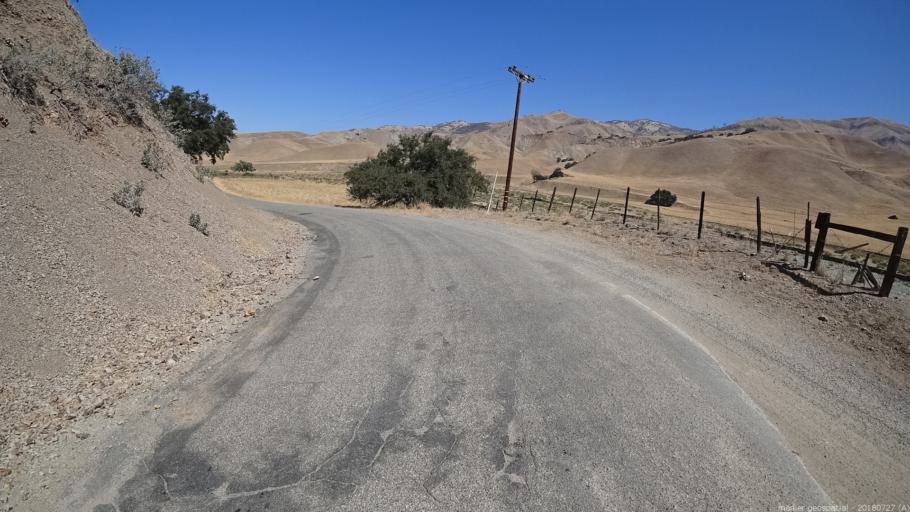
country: US
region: California
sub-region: Monterey County
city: King City
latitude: 36.3061
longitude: -120.9113
